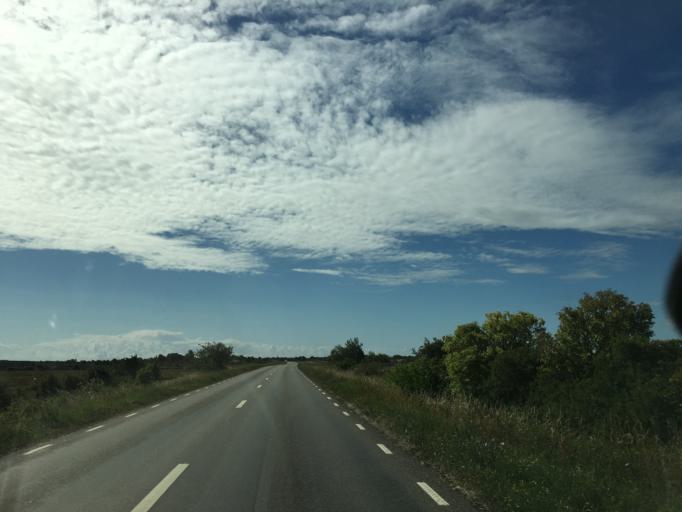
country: SE
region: Kalmar
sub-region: Morbylanga Kommun
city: Moerbylanga
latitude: 56.4931
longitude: 16.4261
